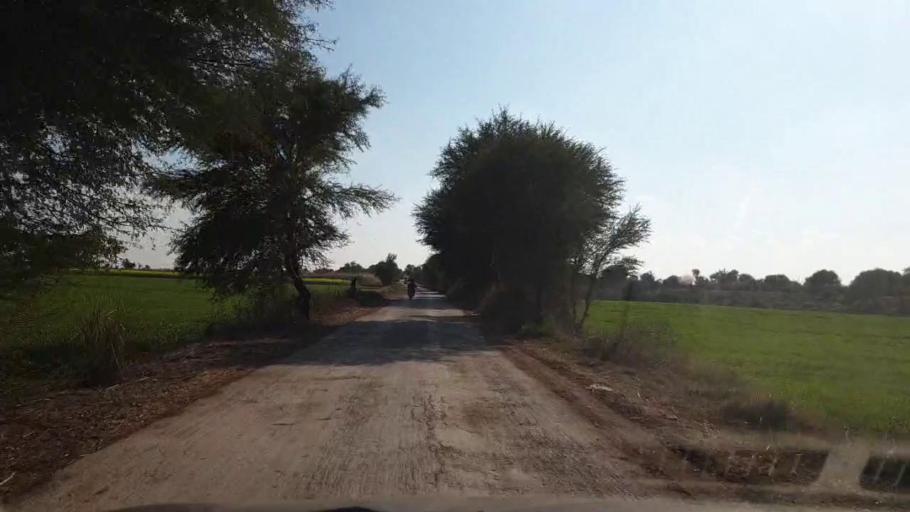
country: PK
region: Sindh
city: Sinjhoro
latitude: 25.9797
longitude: 68.7254
